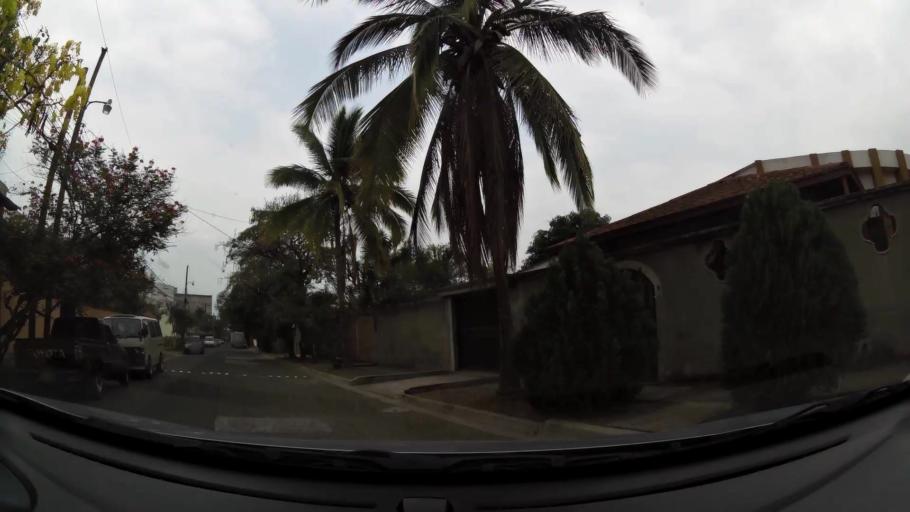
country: HN
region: Francisco Morazan
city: Tegucigalpa
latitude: 14.0978
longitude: -87.1823
